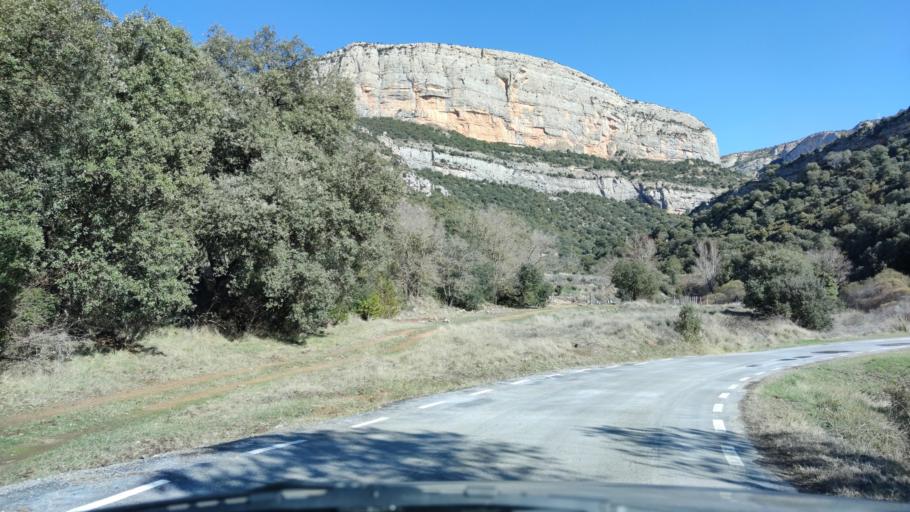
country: ES
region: Catalonia
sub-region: Provincia de Lleida
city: Artesa de Segre
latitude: 42.0136
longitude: 1.0303
